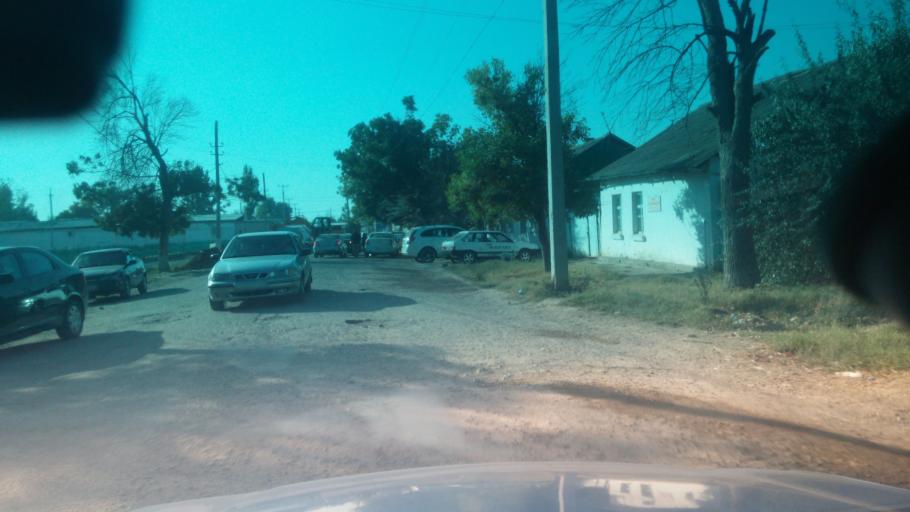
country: UZ
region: Sirdaryo
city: Guliston
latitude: 40.4957
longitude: 68.7694
